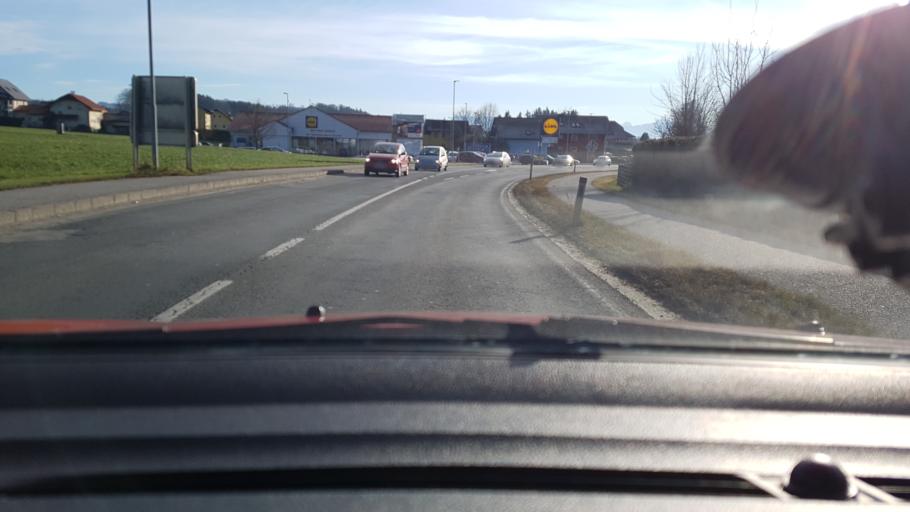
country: AT
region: Salzburg
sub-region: Politischer Bezirk Salzburg-Umgebung
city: Lamprechtshausen
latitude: 47.9899
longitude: 12.9553
